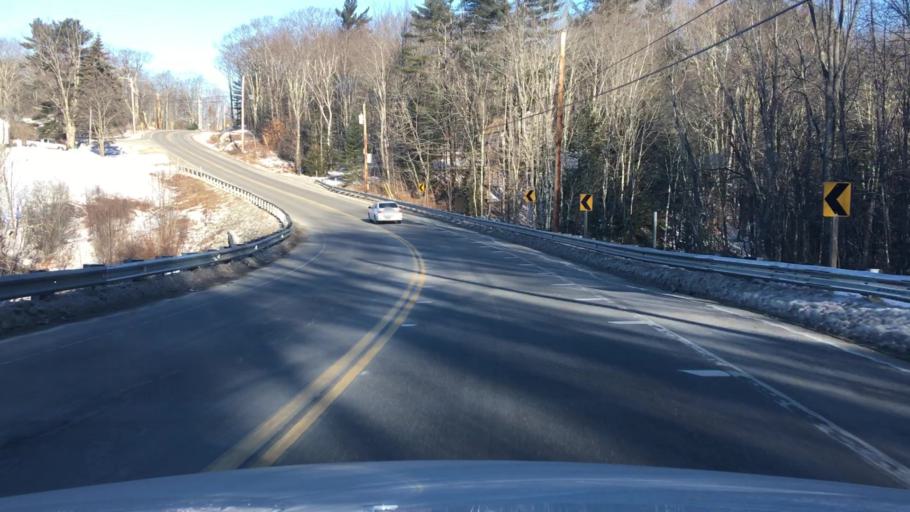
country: US
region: Maine
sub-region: Cumberland County
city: Freeport
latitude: 43.8987
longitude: -70.1140
